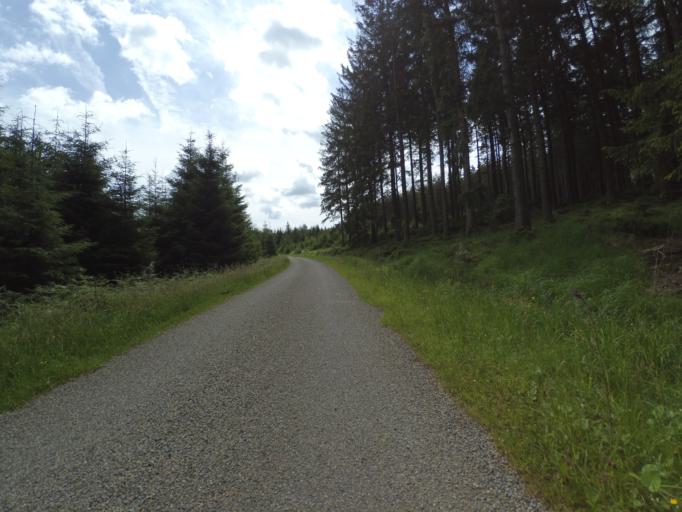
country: BE
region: Wallonia
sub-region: Province de Liege
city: Raeren
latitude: 50.5948
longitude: 6.1313
